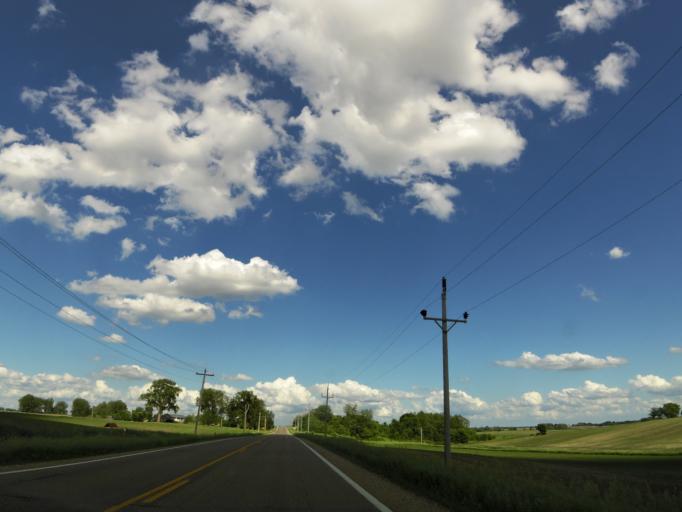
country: US
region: Minnesota
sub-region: Wright County
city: Cokato
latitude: 45.0658
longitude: -94.2199
